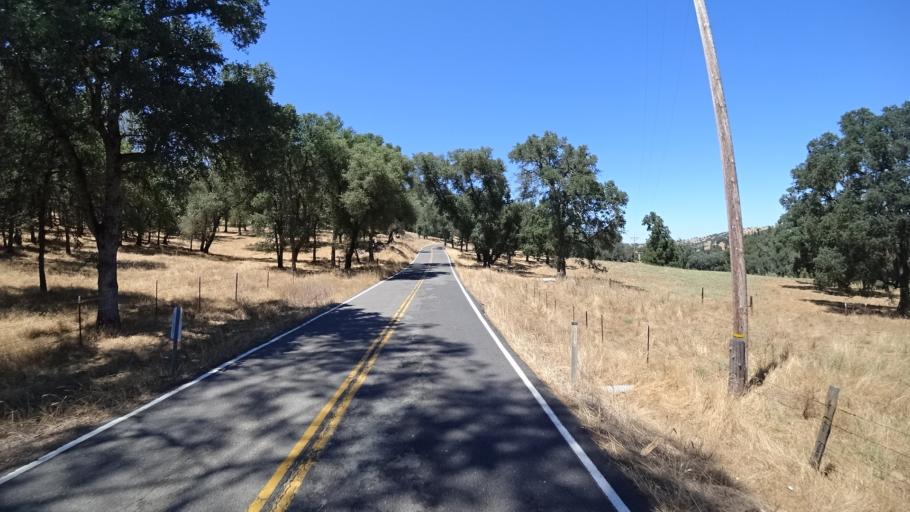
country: US
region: California
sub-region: Calaveras County
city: San Andreas
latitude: 38.1293
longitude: -120.6628
